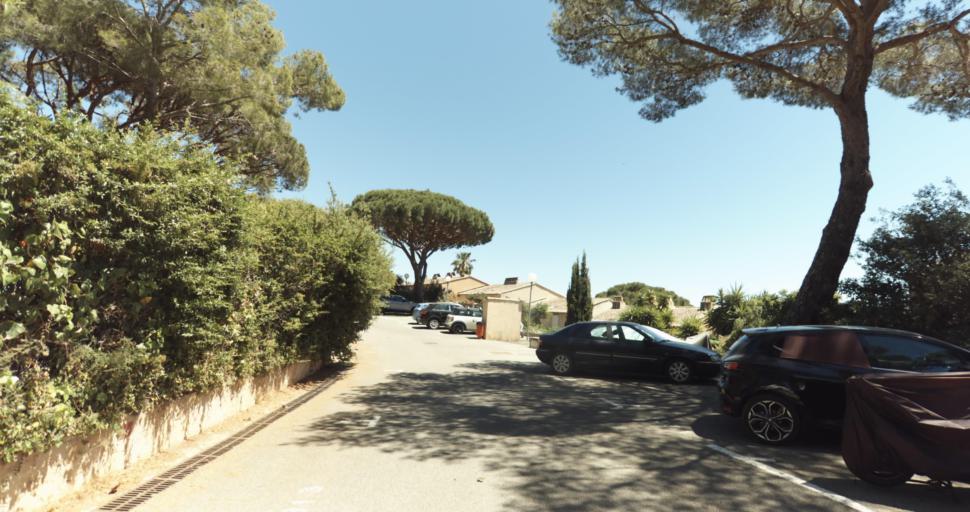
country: FR
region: Provence-Alpes-Cote d'Azur
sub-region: Departement du Var
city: Gassin
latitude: 43.2582
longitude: 6.5735
